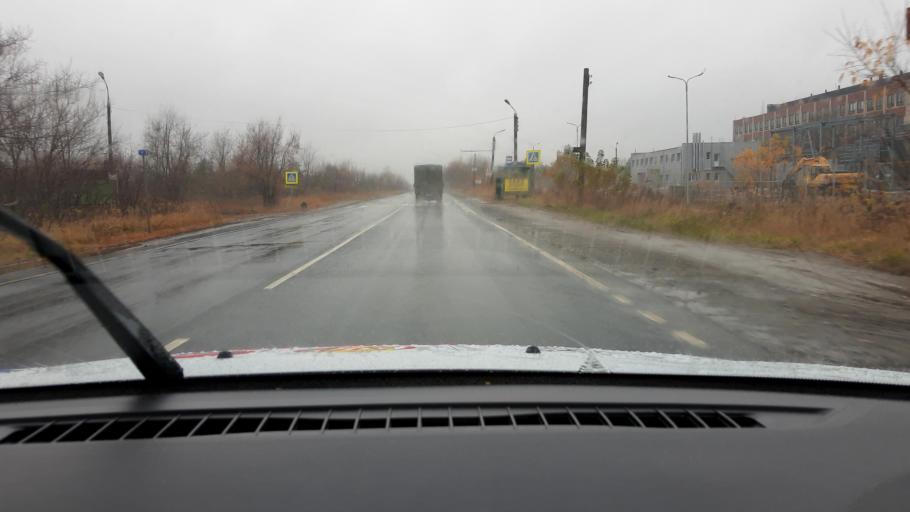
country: RU
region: Nizjnij Novgorod
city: Babino
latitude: 56.2579
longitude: 43.6300
